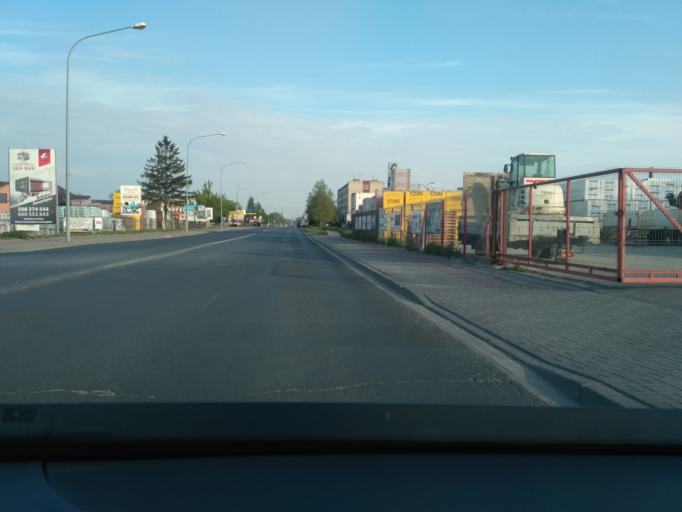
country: PL
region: Masovian Voivodeship
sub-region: Siedlce
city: Siedlce
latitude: 52.1557
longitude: 22.2961
